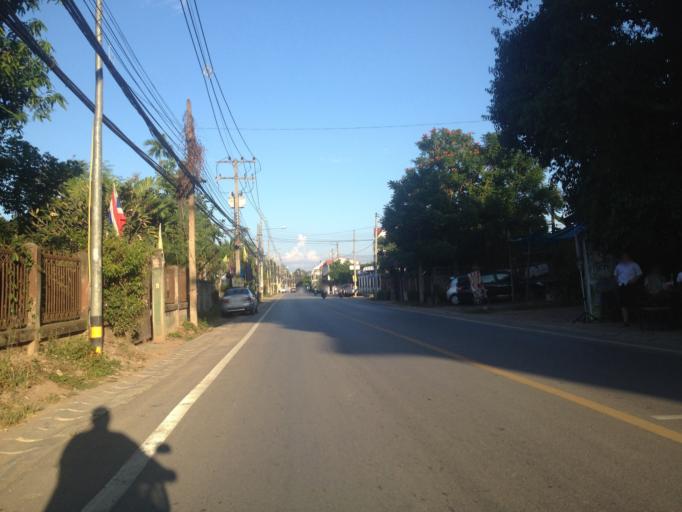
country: TH
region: Chiang Mai
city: San Pa Tong
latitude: 18.6241
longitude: 98.8909
